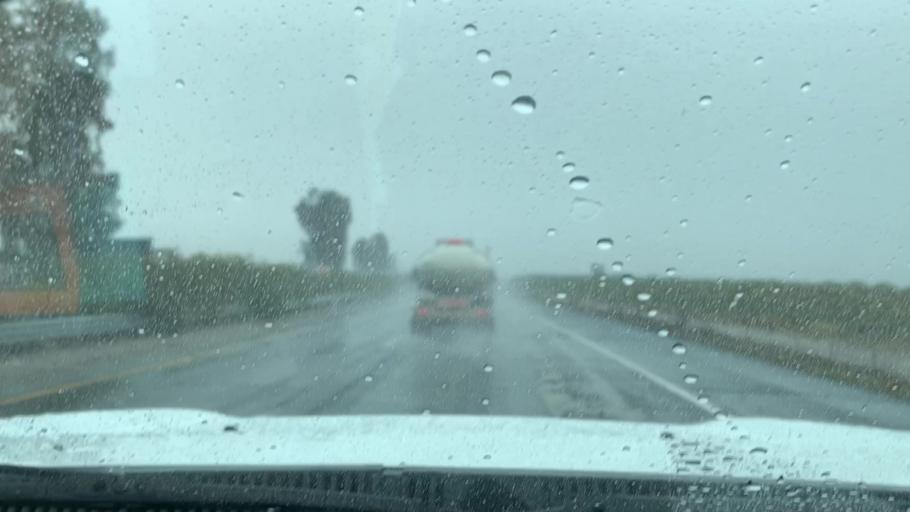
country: US
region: California
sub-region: Tulare County
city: Earlimart
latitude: 35.8388
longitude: -119.2619
